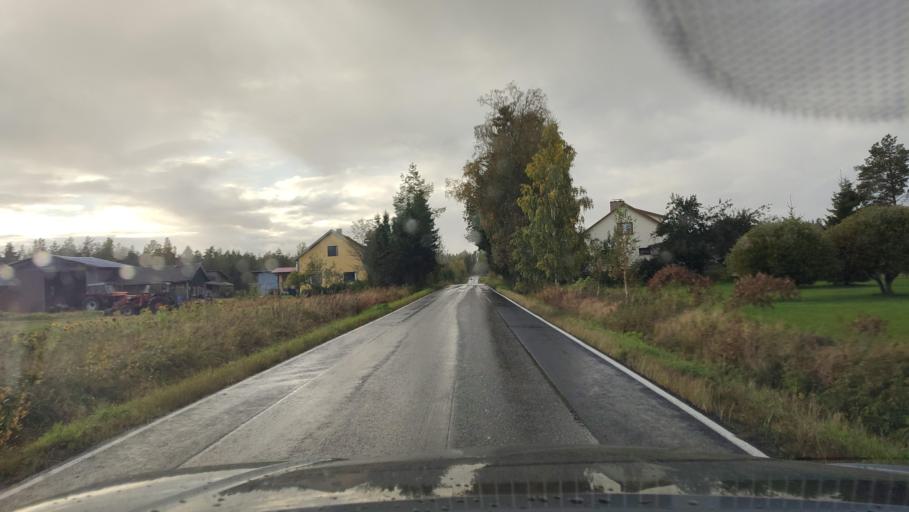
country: FI
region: Southern Ostrobothnia
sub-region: Suupohja
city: Karijoki
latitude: 62.3149
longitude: 21.6943
